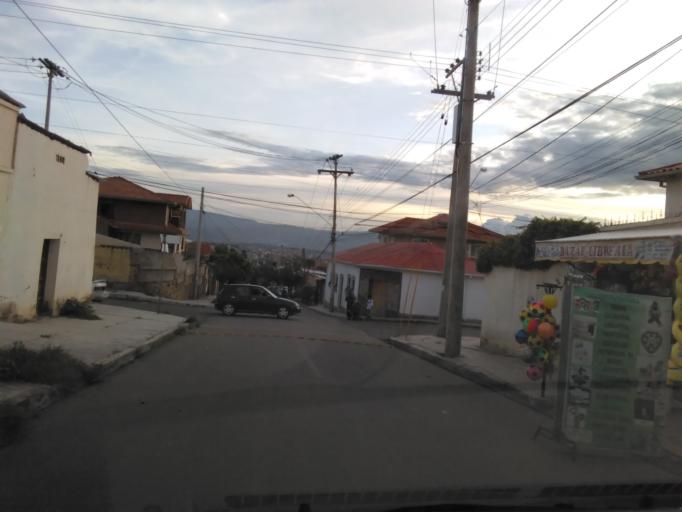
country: BO
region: Cochabamba
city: Cochabamba
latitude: -17.3604
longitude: -66.1618
